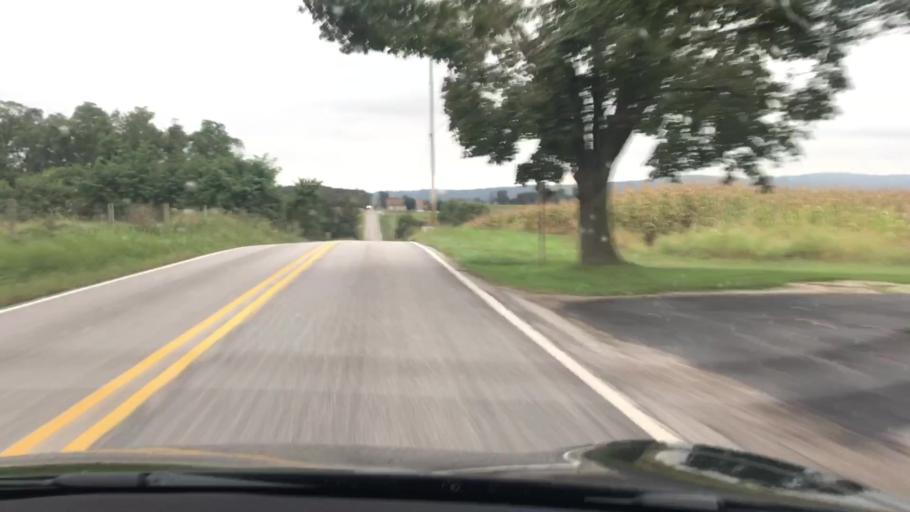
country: US
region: Pennsylvania
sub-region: York County
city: Dover
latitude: 39.9650
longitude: -76.8731
